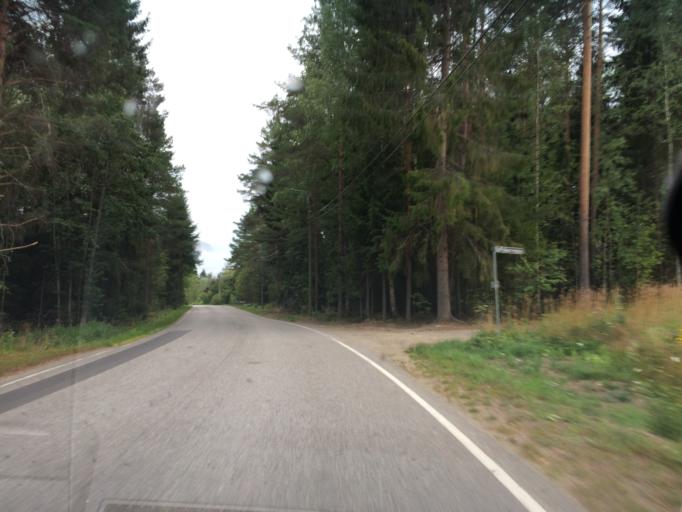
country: FI
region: Haeme
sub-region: Haemeenlinna
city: Tuulos
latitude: 61.1786
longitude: 24.7578
